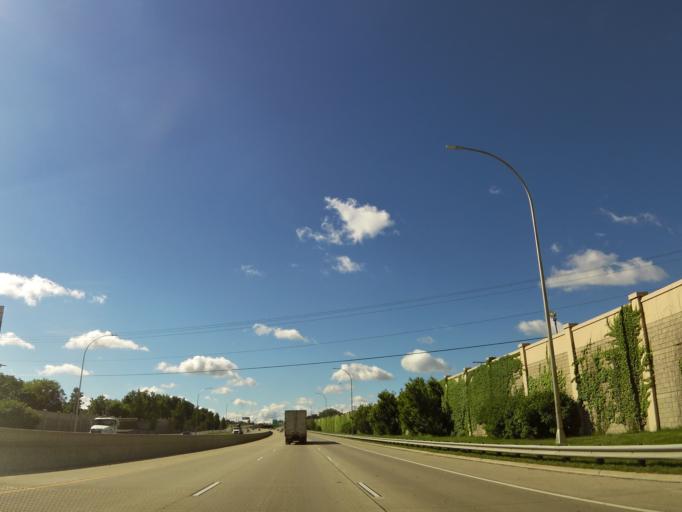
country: US
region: Minnesota
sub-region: Olmsted County
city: Rochester
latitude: 44.0513
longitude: -92.4930
